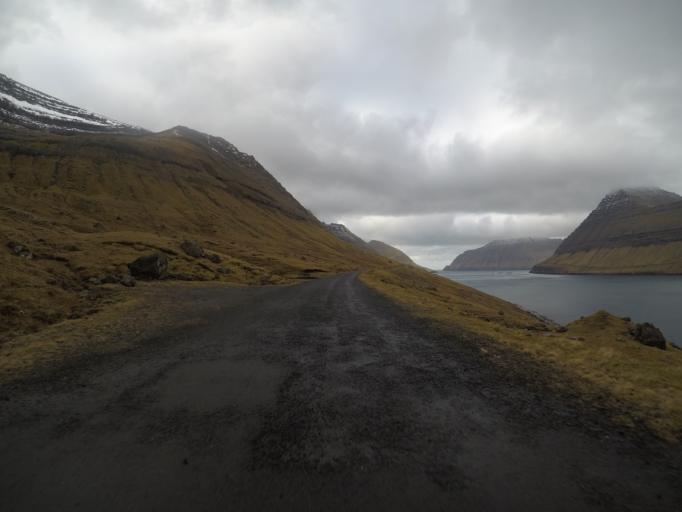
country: FO
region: Nordoyar
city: Klaksvik
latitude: 62.3176
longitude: -6.5569
